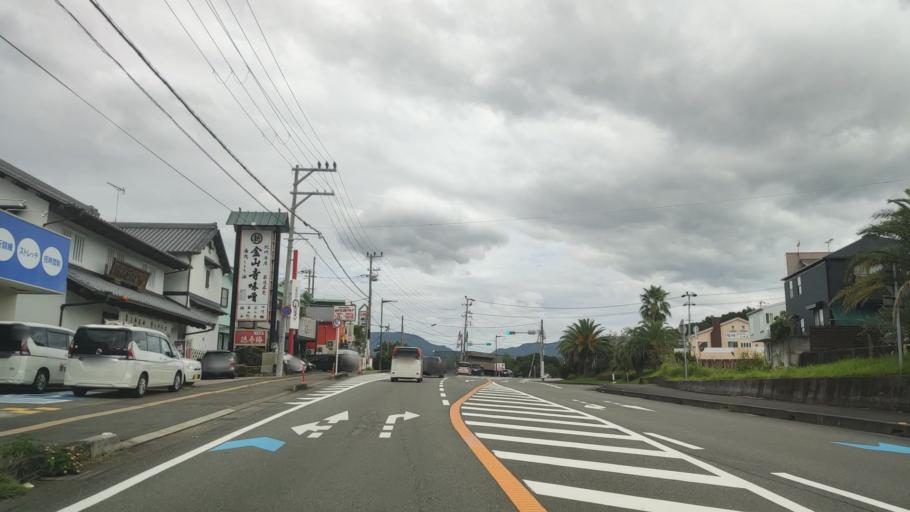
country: JP
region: Wakayama
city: Tanabe
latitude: 33.7075
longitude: 135.4001
